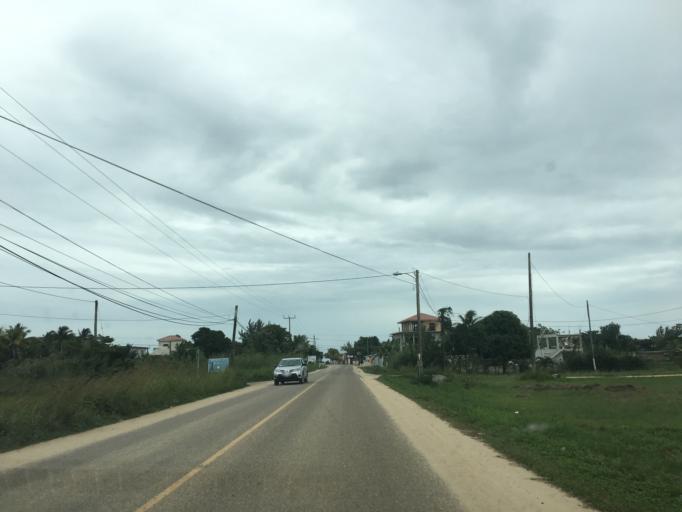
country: BZ
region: Stann Creek
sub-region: Dangriga
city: Dangriga
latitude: 16.8627
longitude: -88.2866
